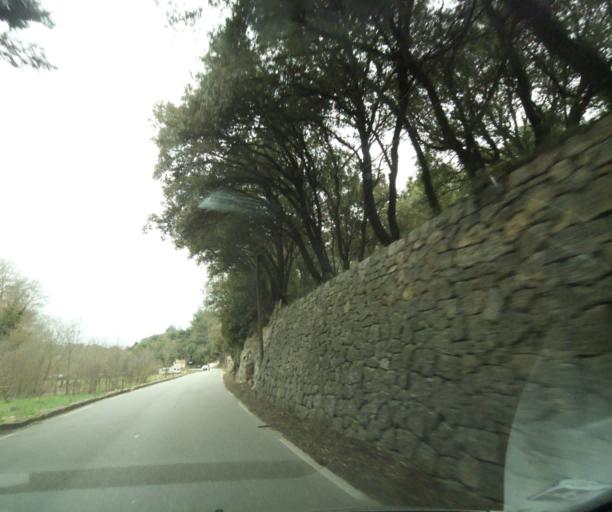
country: FR
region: Provence-Alpes-Cote d'Azur
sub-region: Departement des Bouches-du-Rhone
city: Jouques
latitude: 43.6326
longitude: 5.6478
